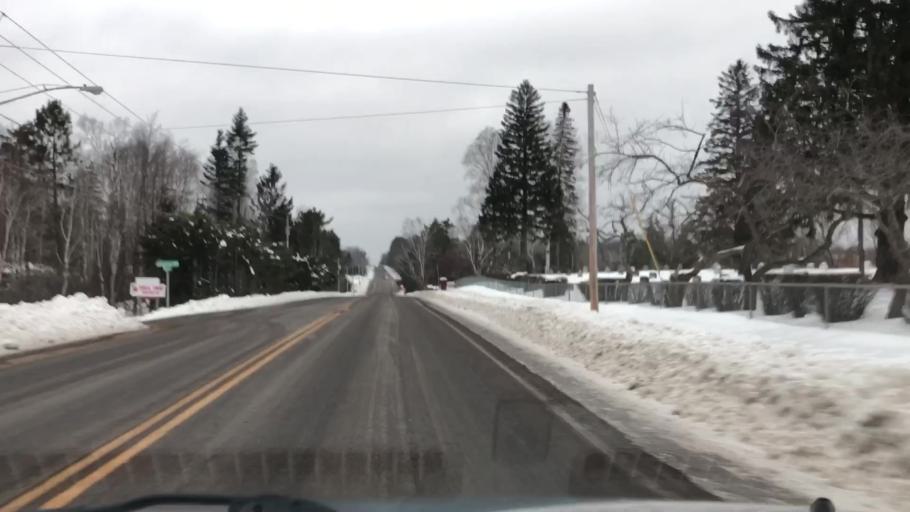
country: US
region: Minnesota
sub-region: Saint Louis County
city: Arnold
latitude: 46.8616
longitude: -92.1111
